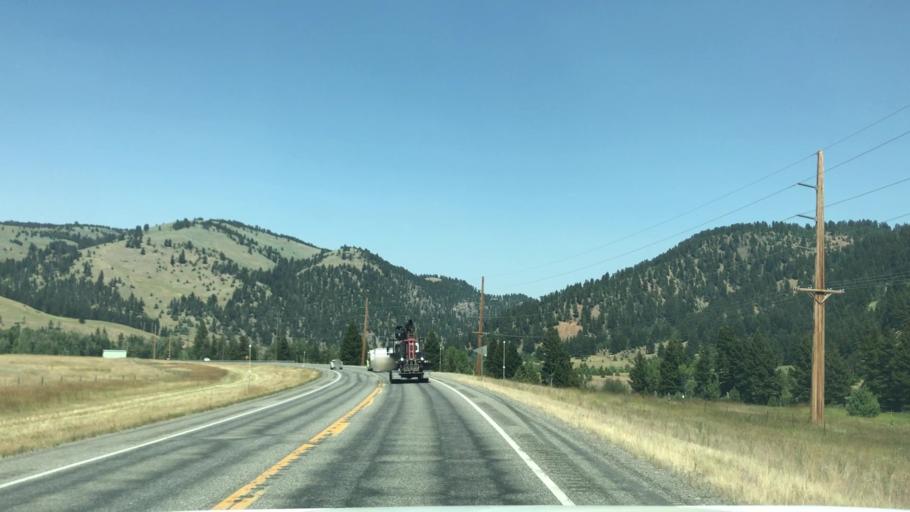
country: US
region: Montana
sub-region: Gallatin County
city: Four Corners
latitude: 45.4863
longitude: -111.2709
